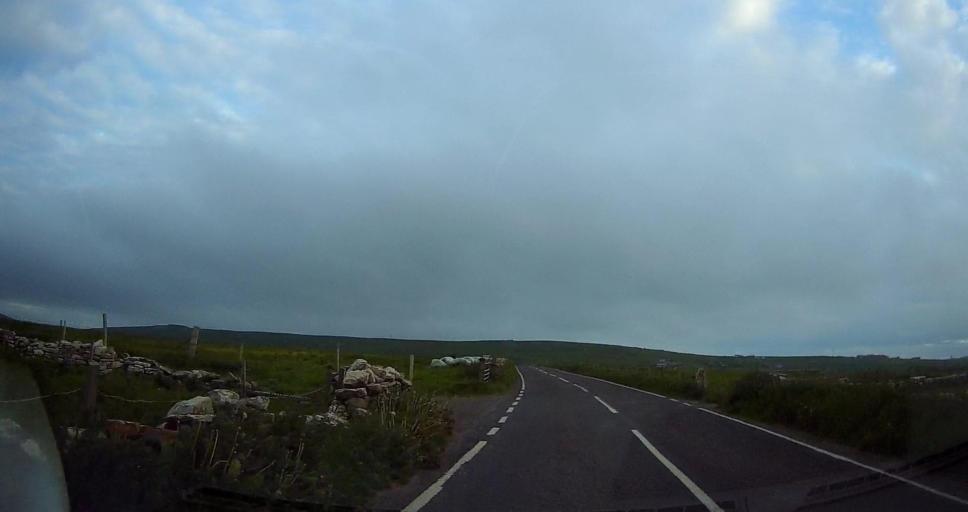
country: GB
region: Scotland
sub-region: Orkney Islands
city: Stromness
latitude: 59.1254
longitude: -3.3045
